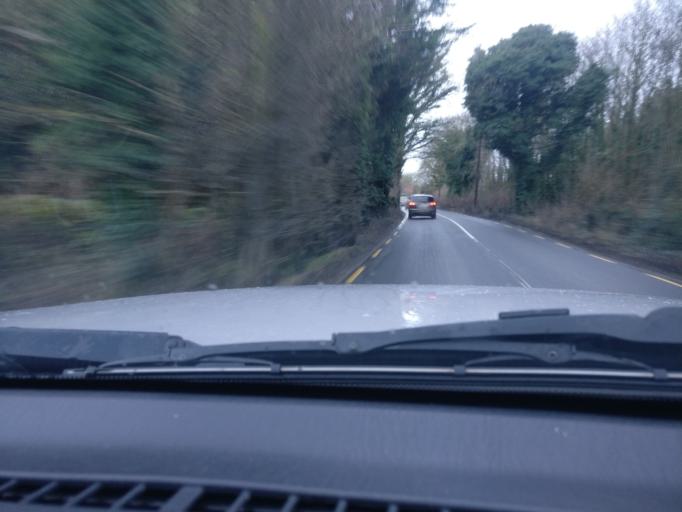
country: IE
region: Leinster
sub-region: An Mhi
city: Longwood
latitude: 53.4846
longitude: -6.8915
